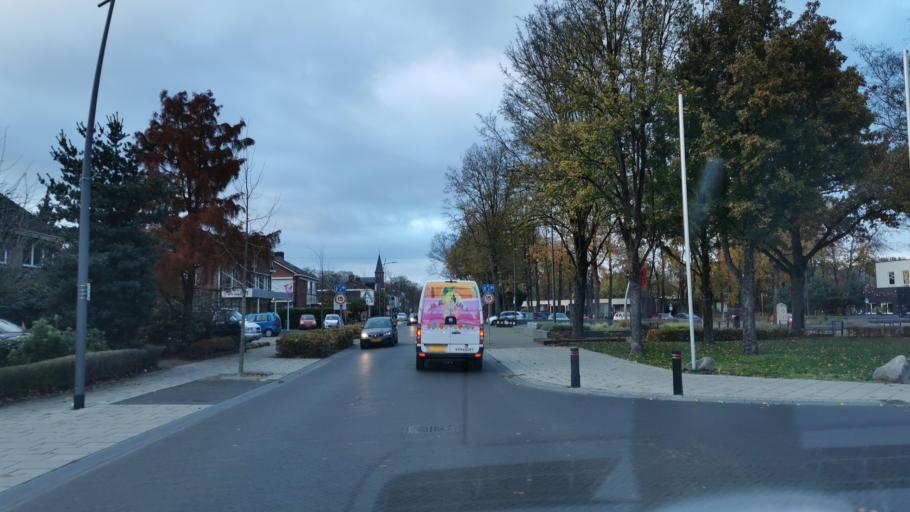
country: DE
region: North Rhine-Westphalia
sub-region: Regierungsbezirk Munster
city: Gronau
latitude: 52.2379
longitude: 7.0346
